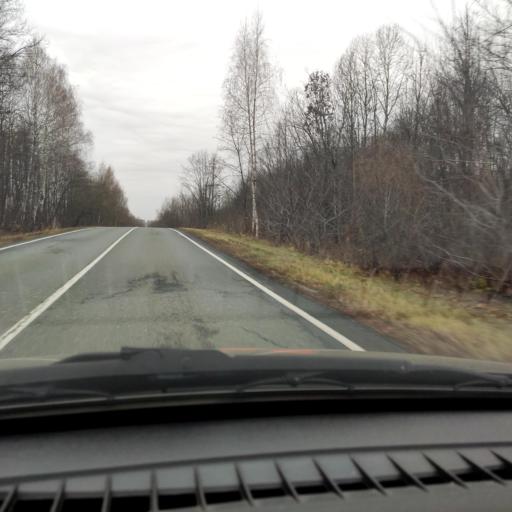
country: RU
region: Samara
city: Zhigulevsk
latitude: 53.3494
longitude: 49.5866
